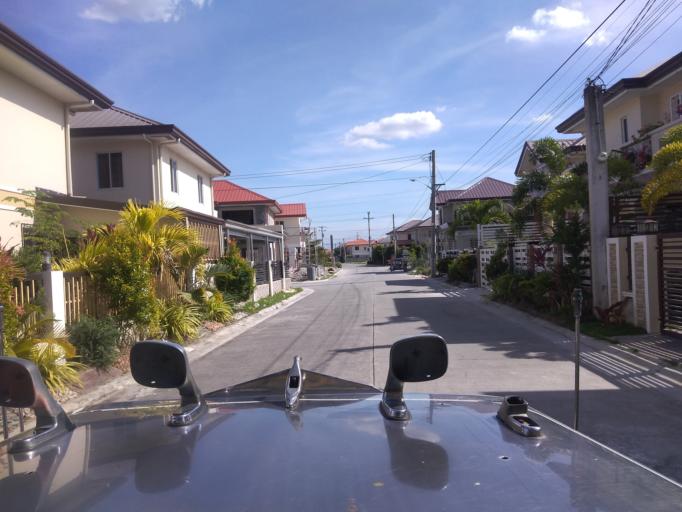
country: PH
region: Central Luzon
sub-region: Province of Pampanga
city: Magliman
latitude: 15.0240
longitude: 120.6591
